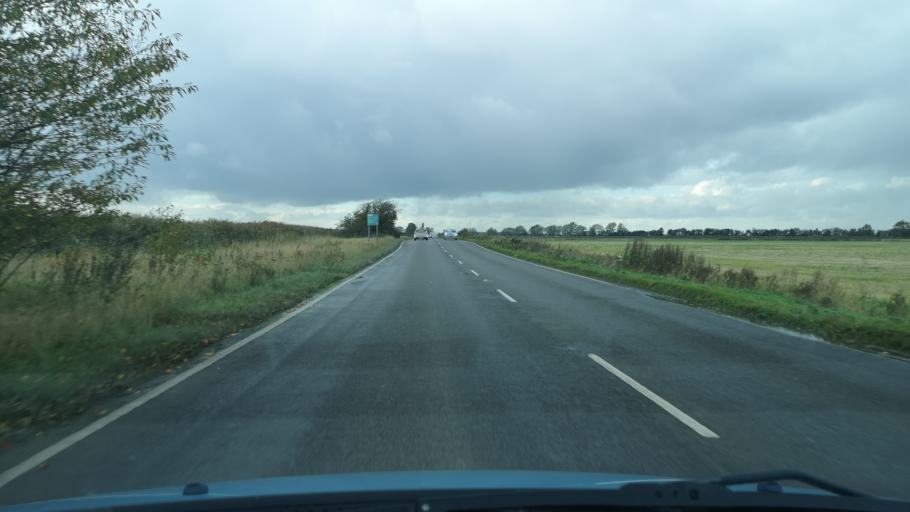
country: GB
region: England
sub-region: North Lincolnshire
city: Gunness
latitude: 53.5777
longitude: -0.7637
